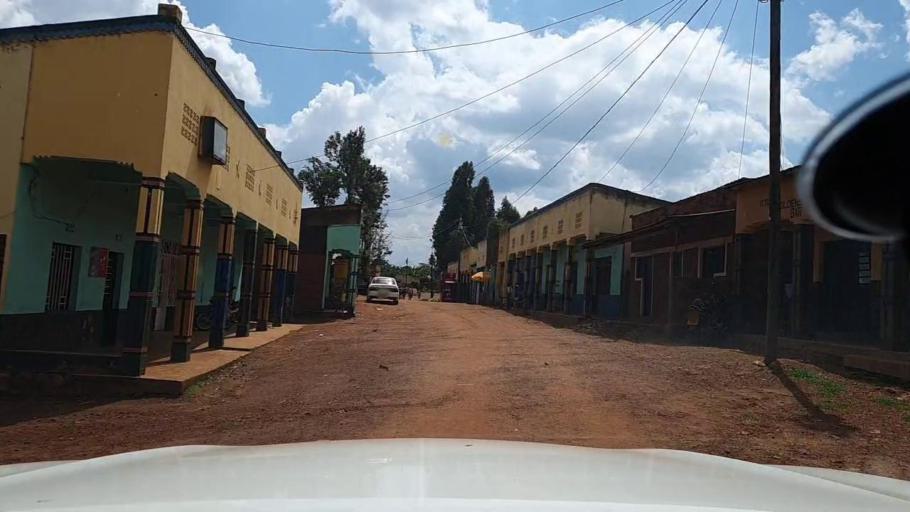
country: RW
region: Southern Province
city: Gitarama
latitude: -1.8356
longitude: 29.8338
